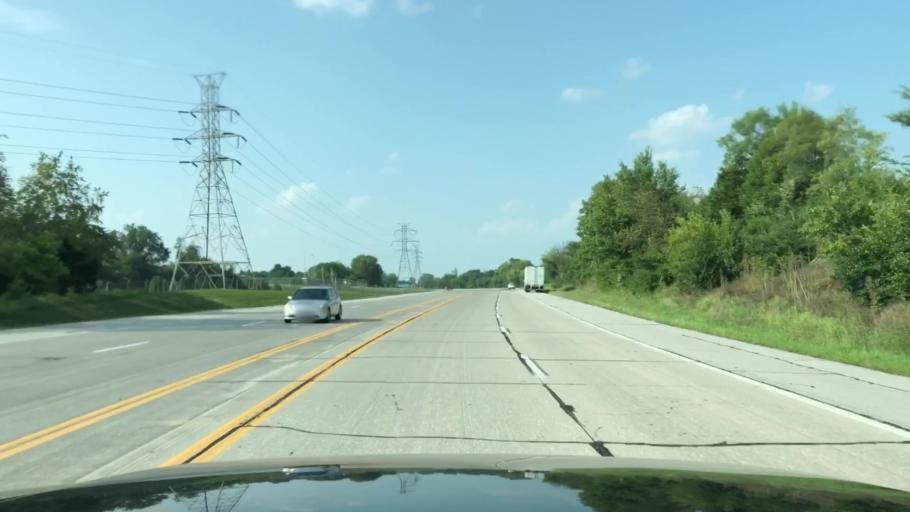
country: US
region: Missouri
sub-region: Saint Charles County
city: Lake Saint Louis
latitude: 38.8145
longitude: -90.8116
